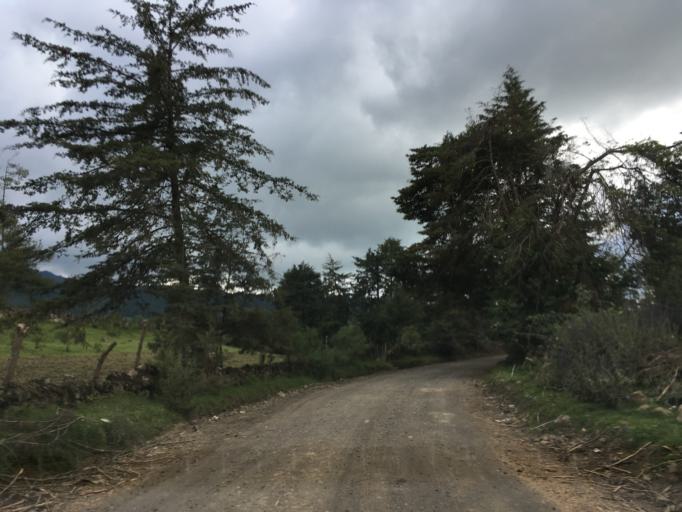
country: MX
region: Michoacan
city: Capula
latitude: 19.6478
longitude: -101.8274
